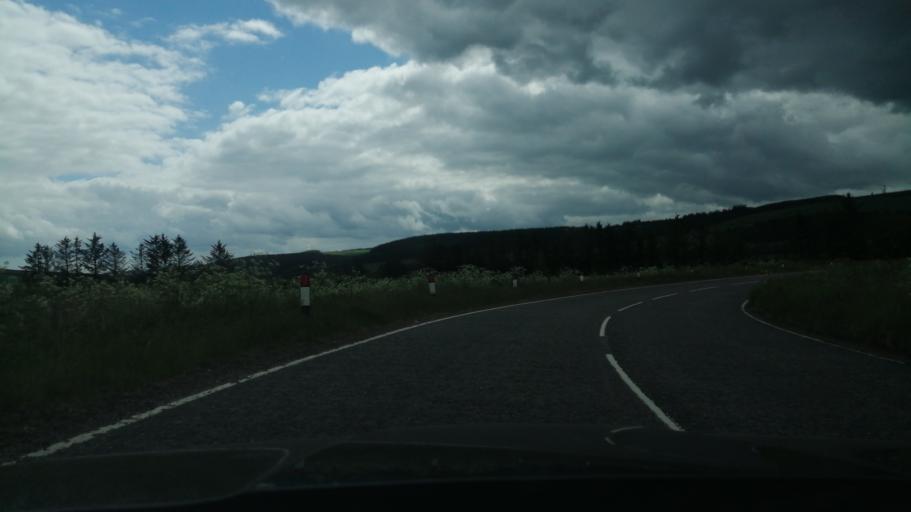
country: GB
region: Scotland
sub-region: Moray
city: Fochabers
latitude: 57.5449
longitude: -3.0873
